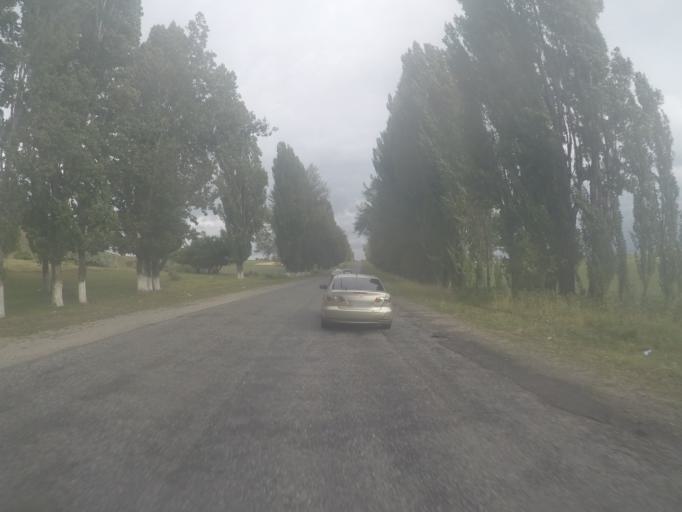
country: KG
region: Ysyk-Koel
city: Tyup
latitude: 42.7438
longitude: 78.0517
